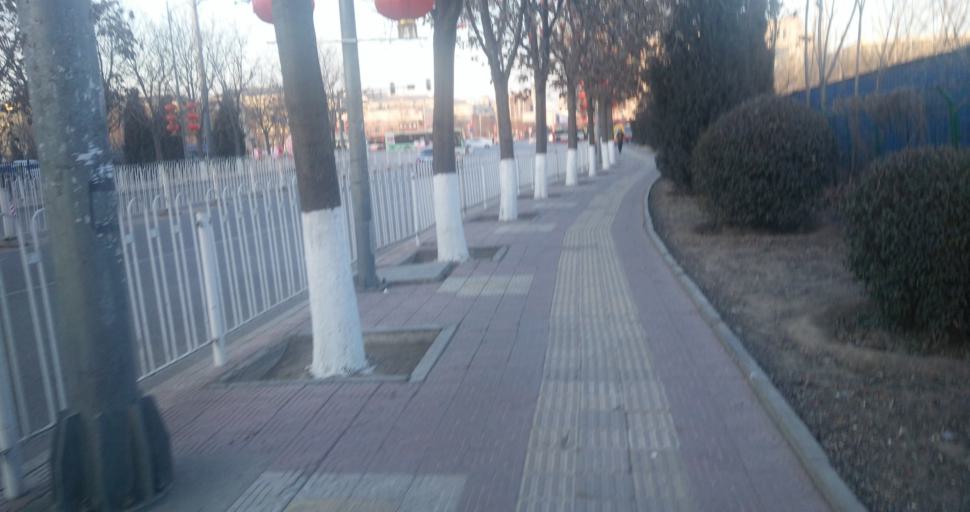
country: CN
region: Beijing
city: Jiugong
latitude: 39.7607
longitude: 116.4972
